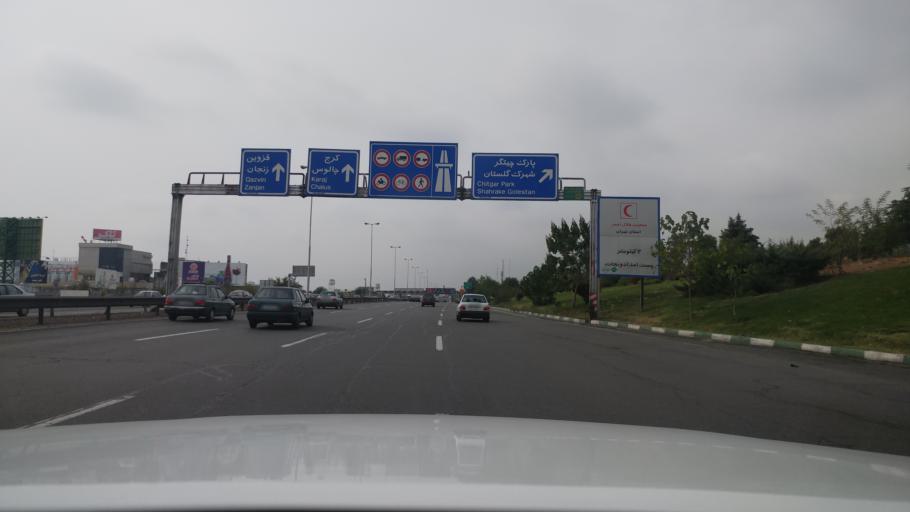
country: IR
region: Tehran
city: Shahr-e Qods
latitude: 35.7152
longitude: 51.2455
